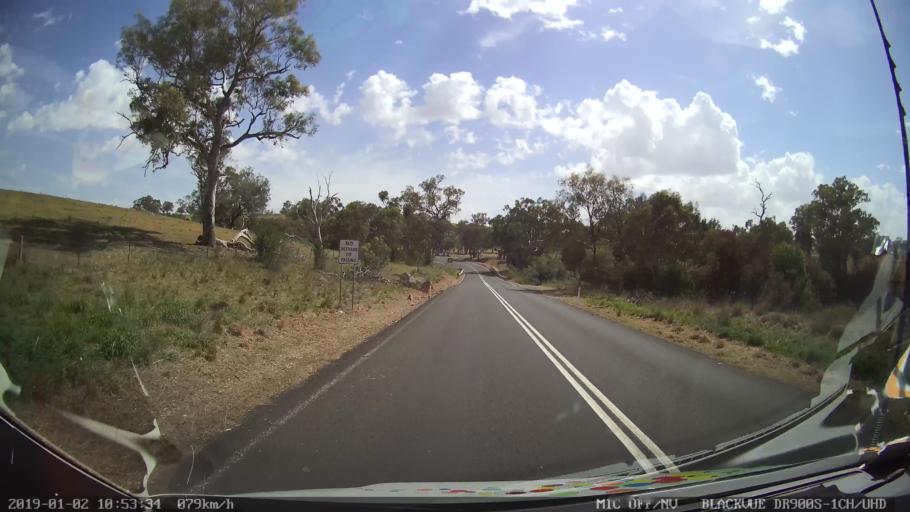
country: AU
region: New South Wales
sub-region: Cootamundra
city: Cootamundra
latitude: -34.6771
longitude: 148.2771
